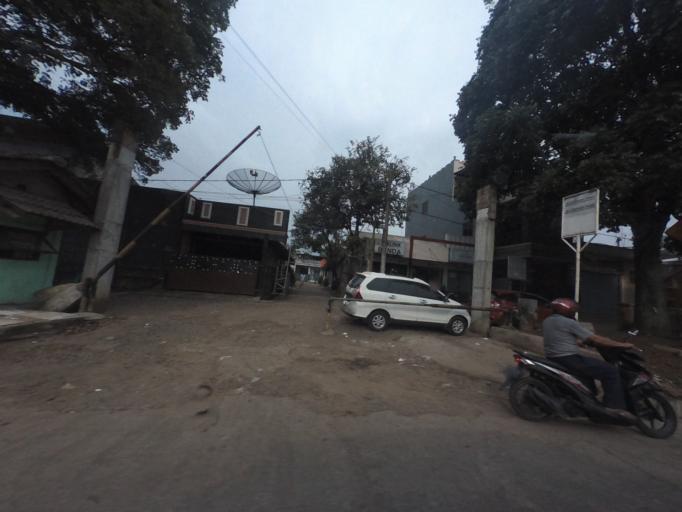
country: ID
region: West Java
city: Cicurug
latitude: -6.7621
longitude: 106.8009
